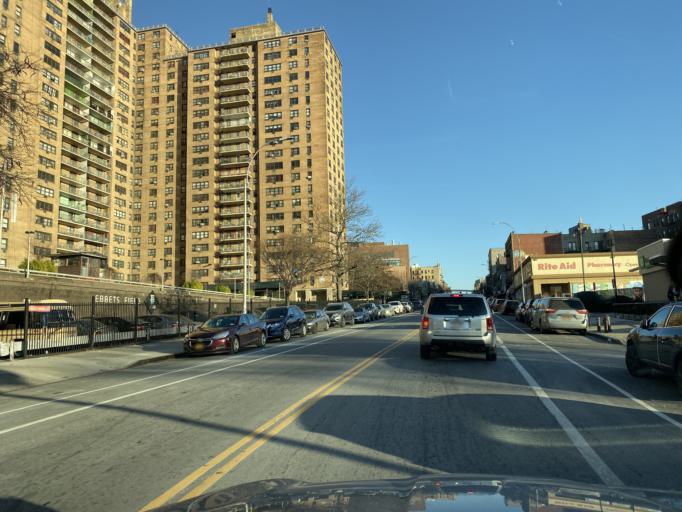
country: US
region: New York
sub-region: Kings County
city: Brooklyn
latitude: 40.6645
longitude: -73.9573
